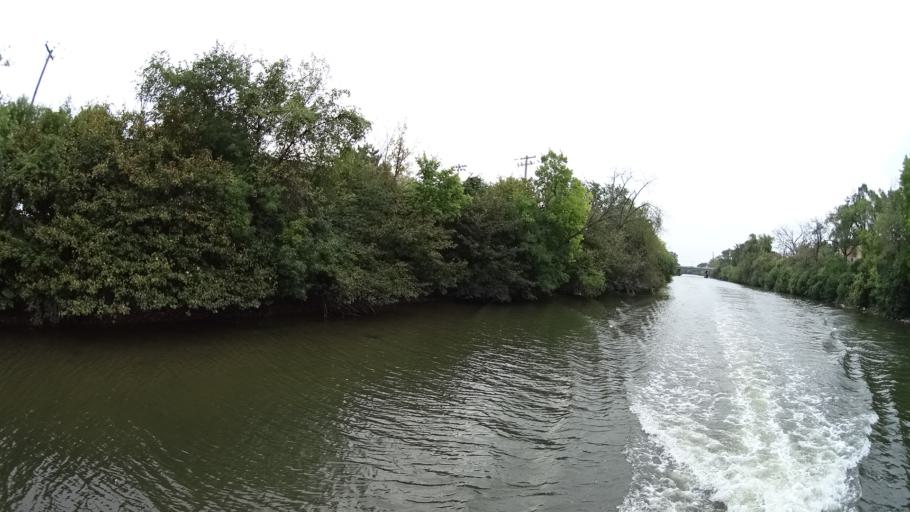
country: US
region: Illinois
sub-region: Cook County
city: Lincolnwood
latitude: 41.9498
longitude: -87.6967
